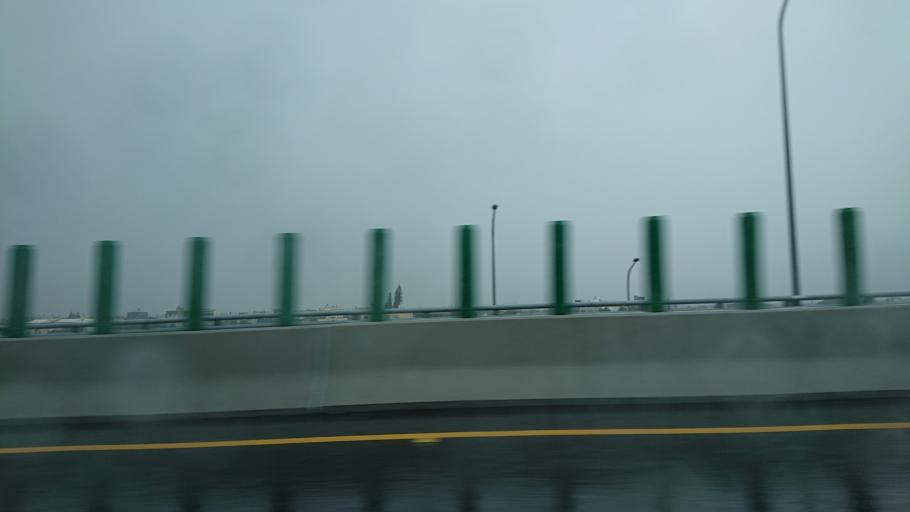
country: TW
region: Taiwan
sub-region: Changhua
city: Chang-hua
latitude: 23.9403
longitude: 120.3228
